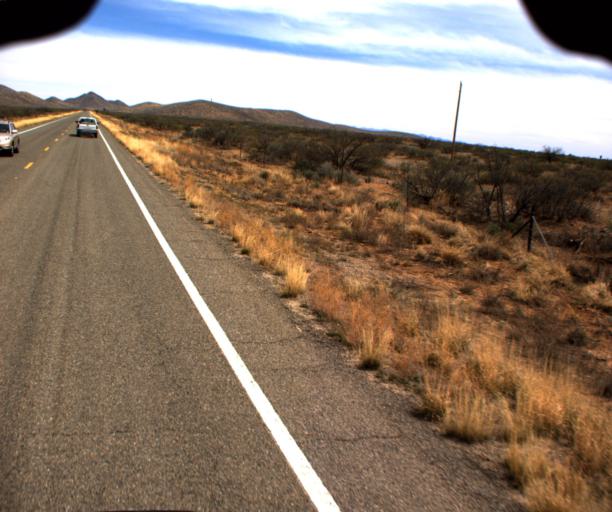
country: US
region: Arizona
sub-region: Cochise County
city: Willcox
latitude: 32.1930
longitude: -109.7014
